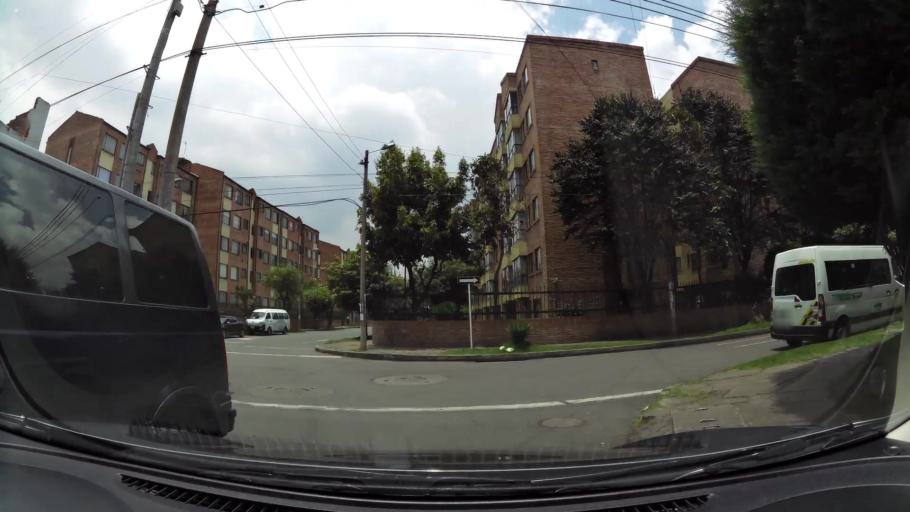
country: CO
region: Cundinamarca
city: Cota
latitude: 4.7507
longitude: -74.0500
